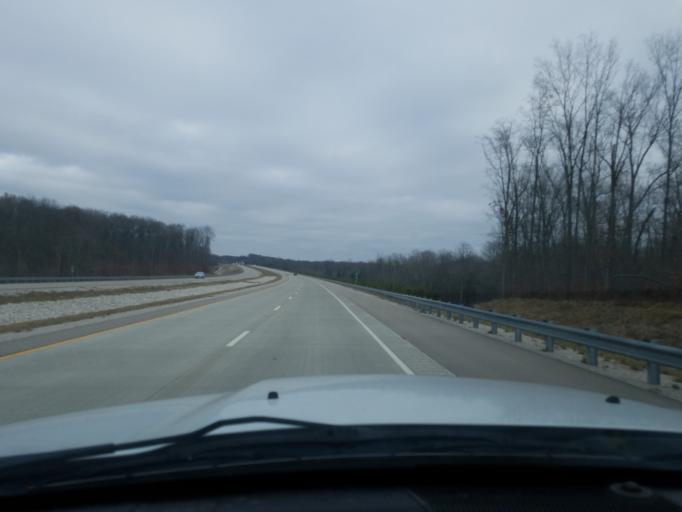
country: US
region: Indiana
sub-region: Monroe County
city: Bloomington
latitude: 39.0711
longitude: -86.6110
